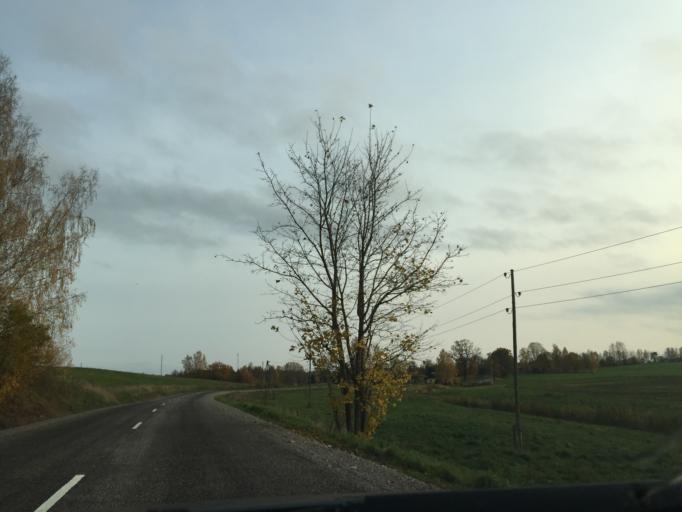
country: LV
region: Pargaujas
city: Stalbe
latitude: 57.3241
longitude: 25.1392
